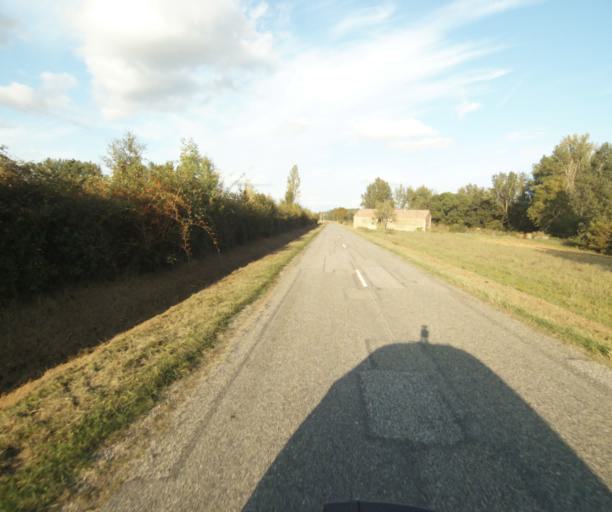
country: FR
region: Midi-Pyrenees
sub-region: Departement de la Haute-Garonne
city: Launac
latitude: 43.8155
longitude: 1.1235
